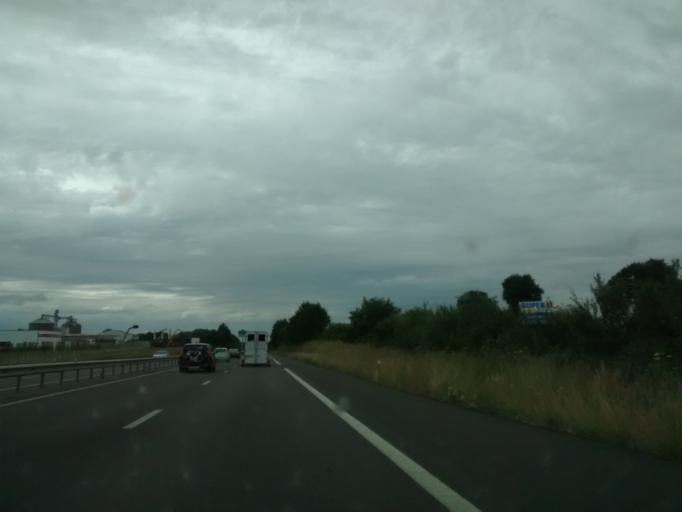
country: FR
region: Brittany
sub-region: Departement des Cotes-d'Armor
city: Broons
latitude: 48.3152
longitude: -2.2448
